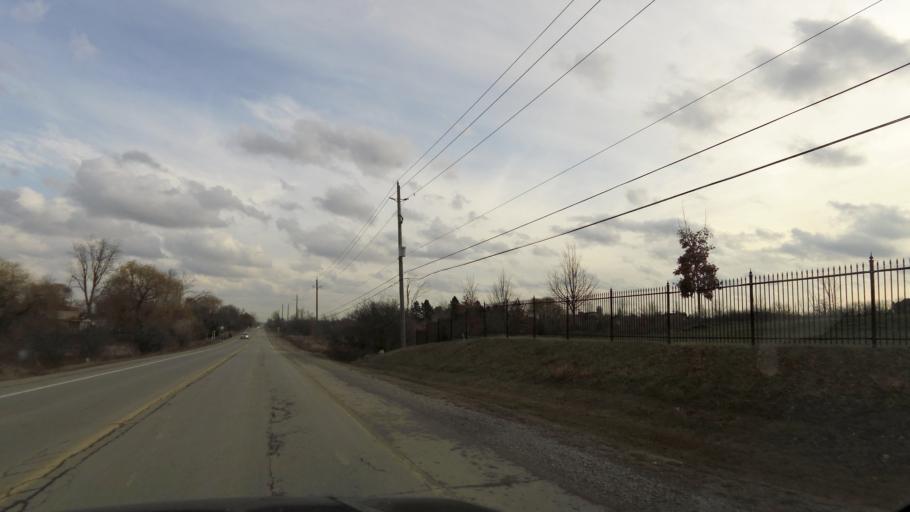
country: CA
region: Ontario
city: Brampton
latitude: 43.7911
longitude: -79.7122
